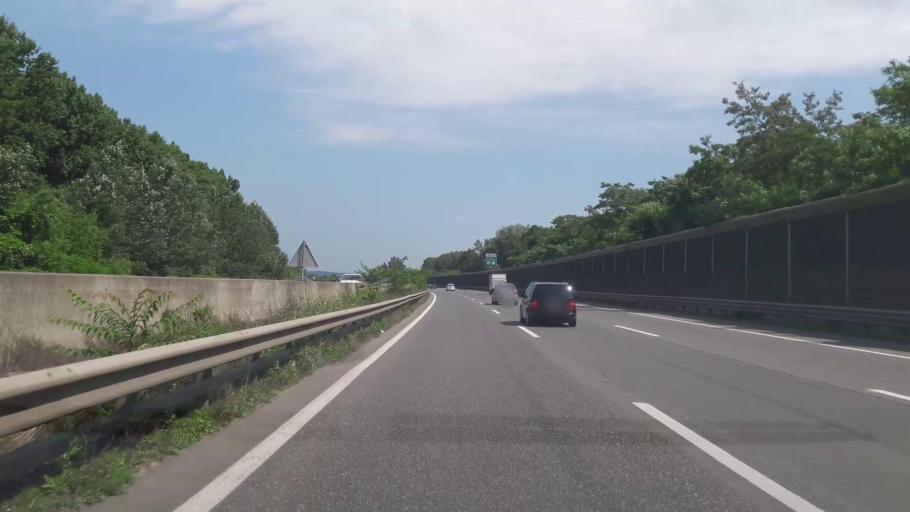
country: AT
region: Lower Austria
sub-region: Politischer Bezirk Korneuburg
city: Langenzersdorf
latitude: 48.3129
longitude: 16.3455
